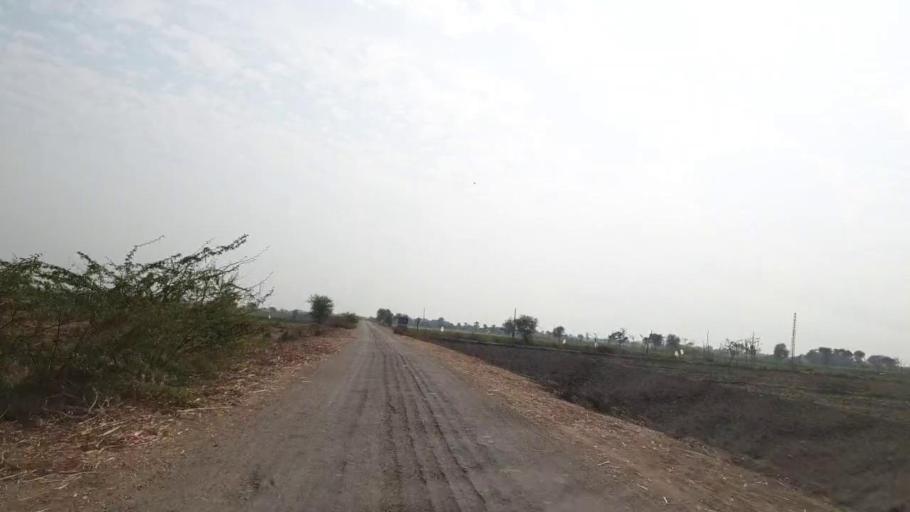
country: PK
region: Sindh
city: Mirpur Khas
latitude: 25.5359
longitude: 69.1572
